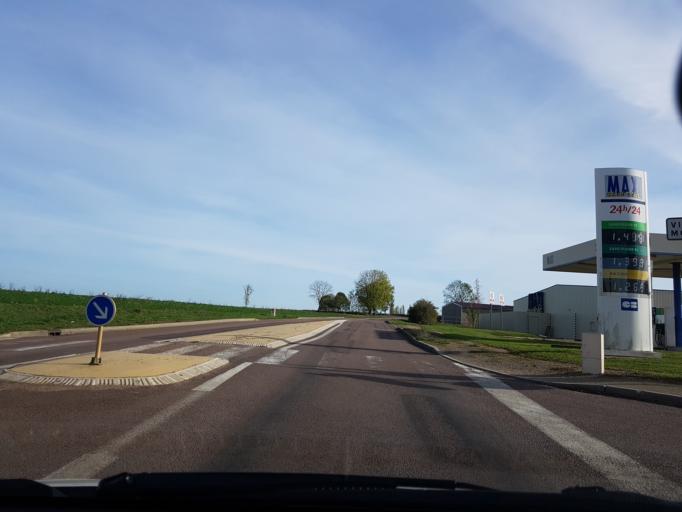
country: FR
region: Bourgogne
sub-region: Departement de la Cote-d'Or
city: Semur-en-Auxois
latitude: 47.4997
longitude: 4.1253
